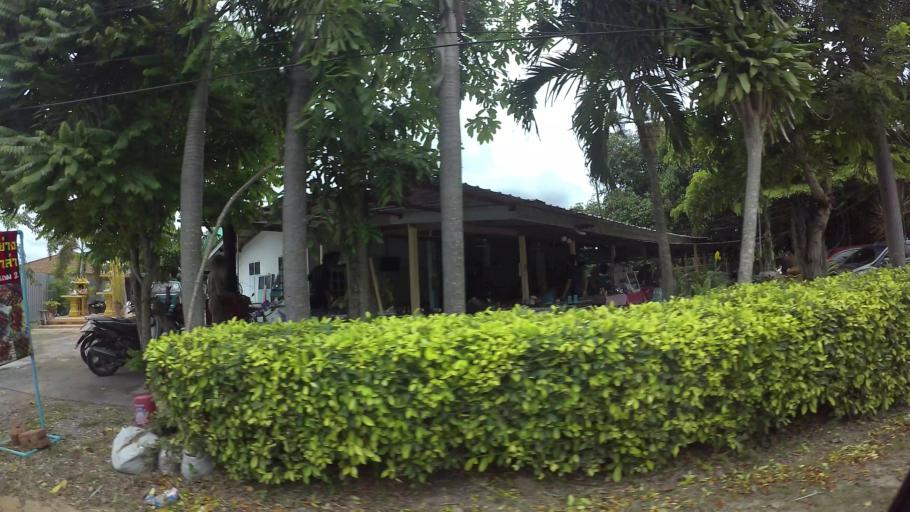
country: TH
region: Chon Buri
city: Si Racha
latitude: 13.1607
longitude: 100.9751
